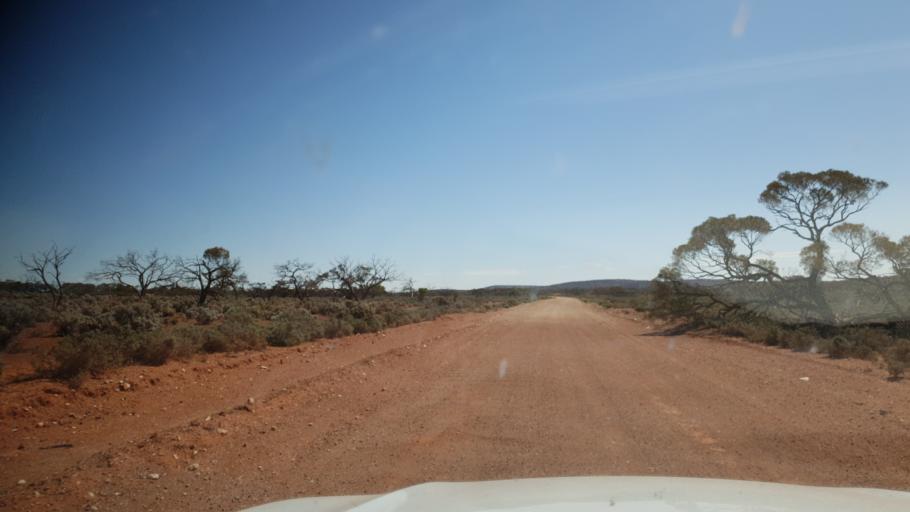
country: AU
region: South Australia
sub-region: Kimba
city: Caralue
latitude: -32.4798
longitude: 136.4321
